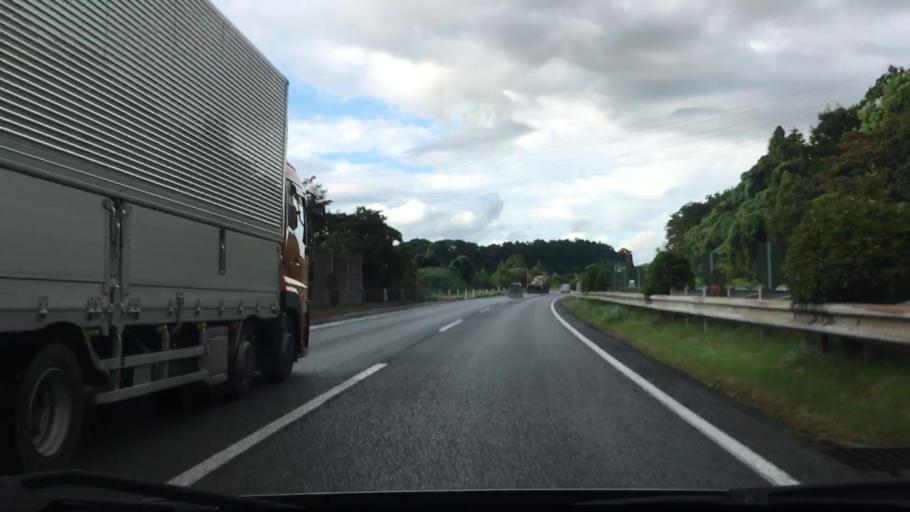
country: JP
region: Fukuoka
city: Koga
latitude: 33.7057
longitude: 130.4856
